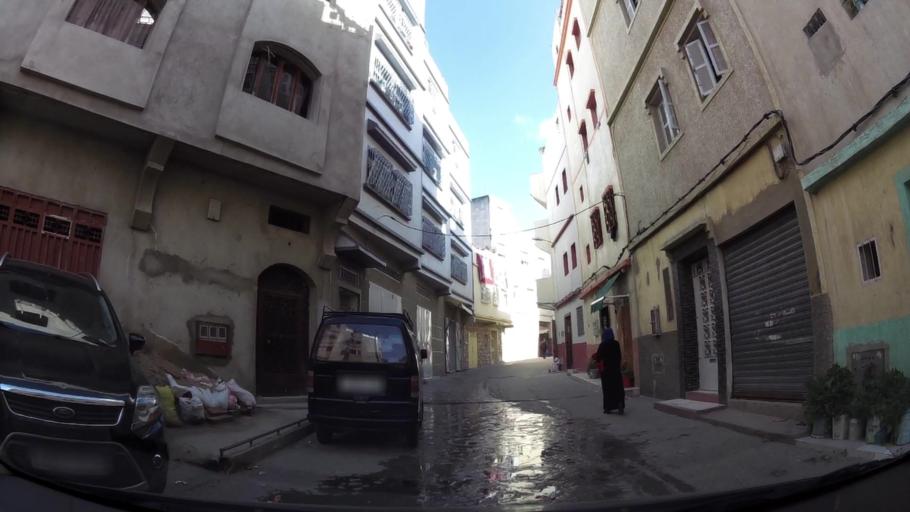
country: MA
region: Tanger-Tetouan
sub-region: Tanger-Assilah
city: Tangier
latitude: 35.7452
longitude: -5.8046
